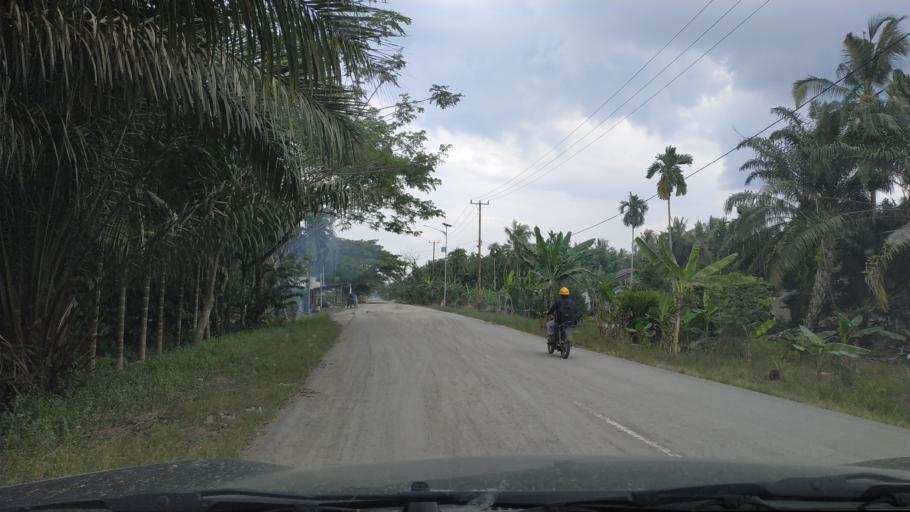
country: ID
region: Riau
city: Sungaisalak
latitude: -0.5652
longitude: 102.9734
